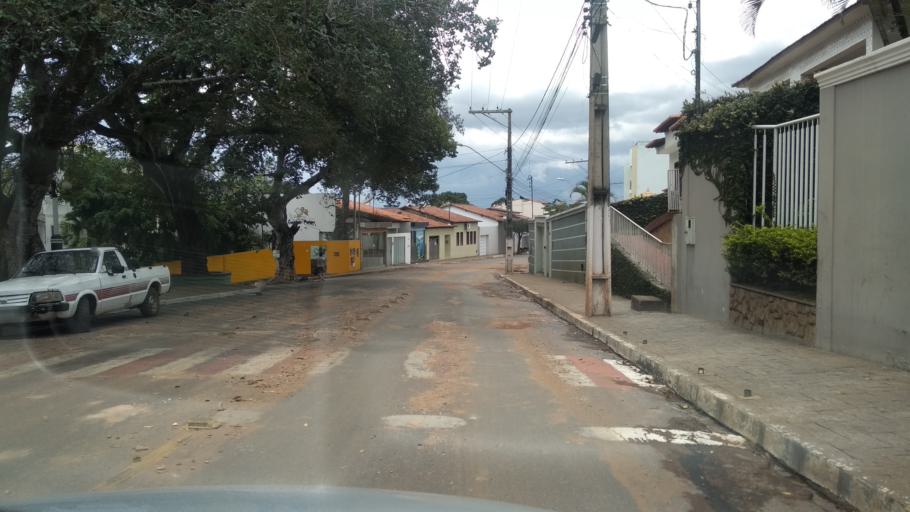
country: BR
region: Bahia
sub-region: Caetite
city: Caetite
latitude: -14.0707
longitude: -42.4913
